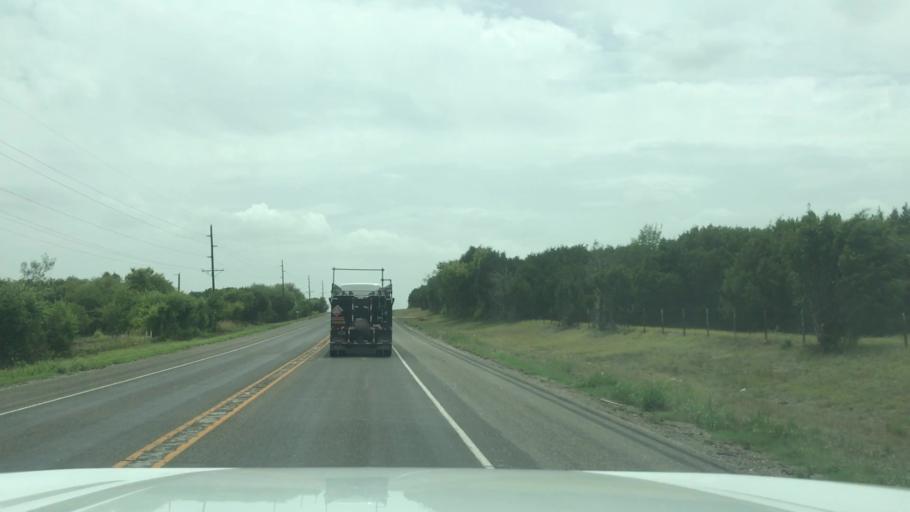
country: US
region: Texas
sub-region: Bosque County
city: Clifton
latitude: 31.7241
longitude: -97.5489
